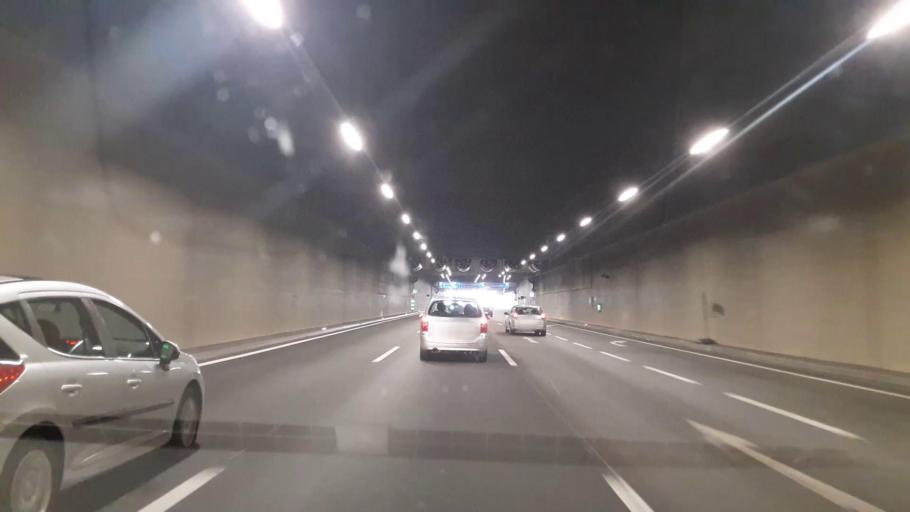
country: AT
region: Vienna
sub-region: Wien Stadt
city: Vienna
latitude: 48.2237
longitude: 16.4217
